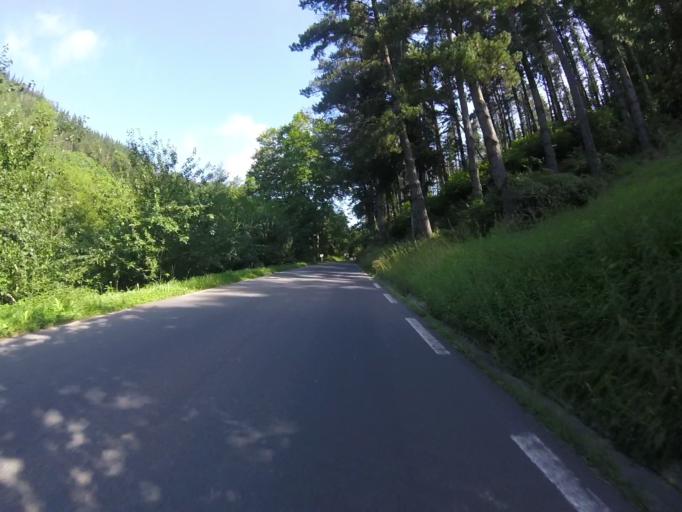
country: ES
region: Basque Country
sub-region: Provincia de Guipuzcoa
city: Ormaiztegui
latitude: 43.0572
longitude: -2.2369
